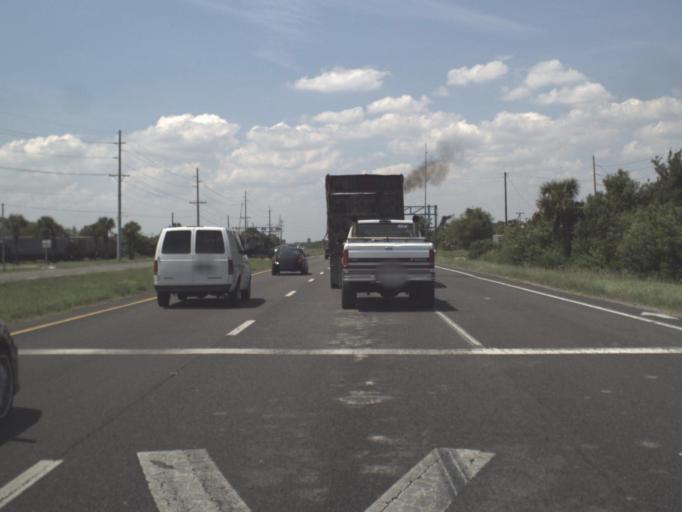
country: US
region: Florida
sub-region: Hillsborough County
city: Gibsonton
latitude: 27.8648
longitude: -82.3852
